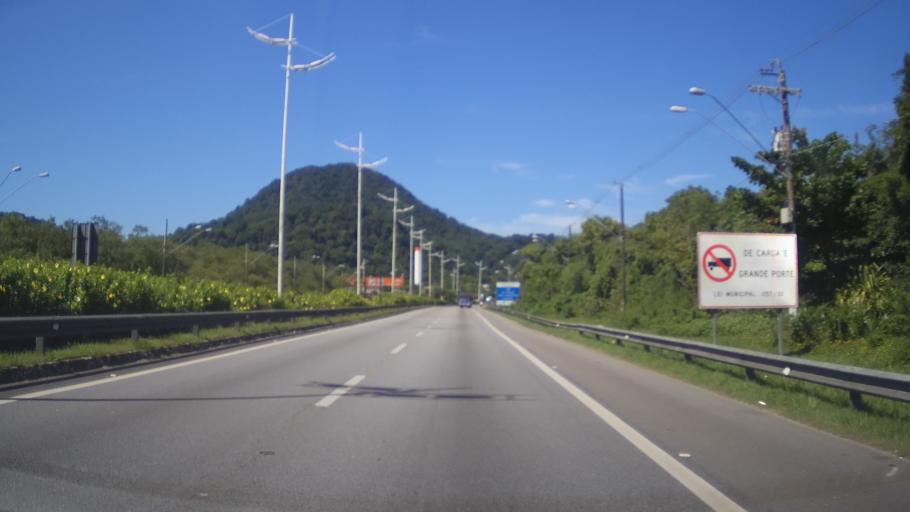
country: BR
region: Sao Paulo
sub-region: Praia Grande
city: Praia Grande
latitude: -23.9855
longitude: -46.4008
